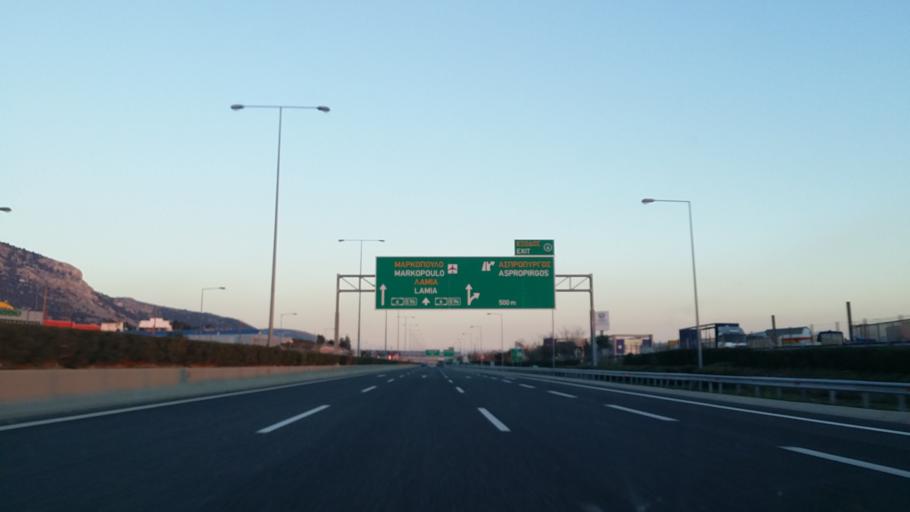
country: GR
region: Attica
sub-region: Nomarchia Dytikis Attikis
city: Aspropyrgos
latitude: 38.0919
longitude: 23.6107
